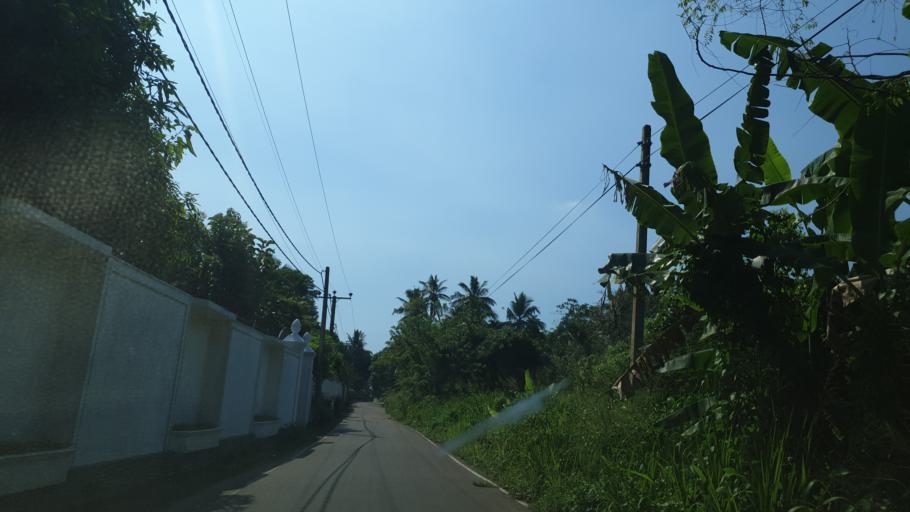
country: LK
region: Western
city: Moratuwa
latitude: 6.7606
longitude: 79.9259
